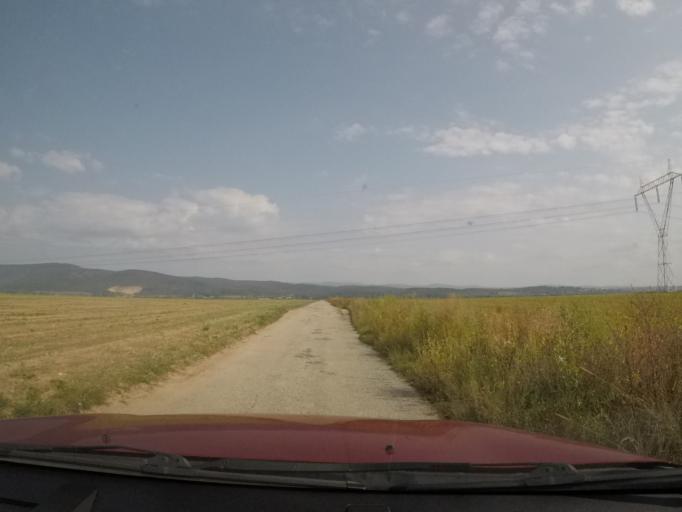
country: SK
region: Kosicky
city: Moldava nad Bodvou
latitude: 48.5862
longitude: 20.9567
